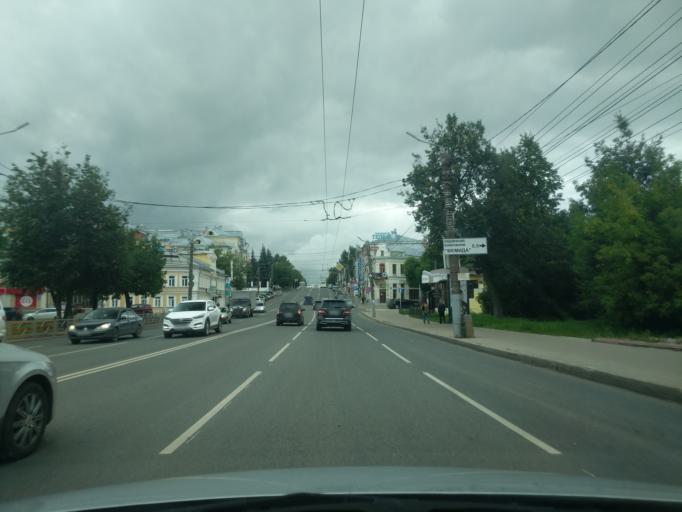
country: RU
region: Kirov
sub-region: Kirovo-Chepetskiy Rayon
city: Kirov
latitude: 58.6002
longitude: 49.6812
